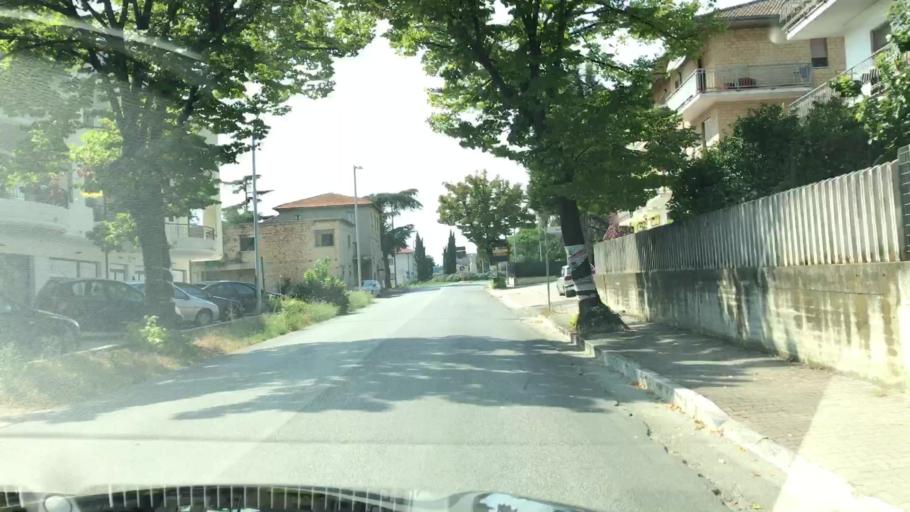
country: IT
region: The Marches
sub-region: Provincia di Ascoli Piceno
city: Pagliare
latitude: 42.8741
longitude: 13.7679
